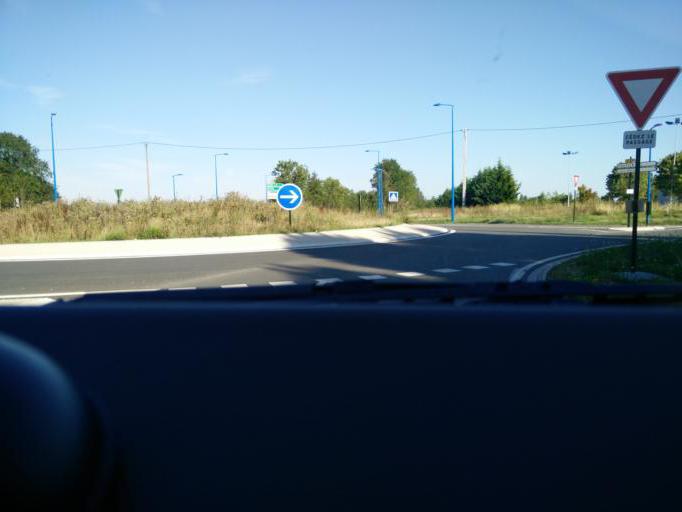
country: FR
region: Nord-Pas-de-Calais
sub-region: Departement du Pas-de-Calais
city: Houdain
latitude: 50.4529
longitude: 2.5451
